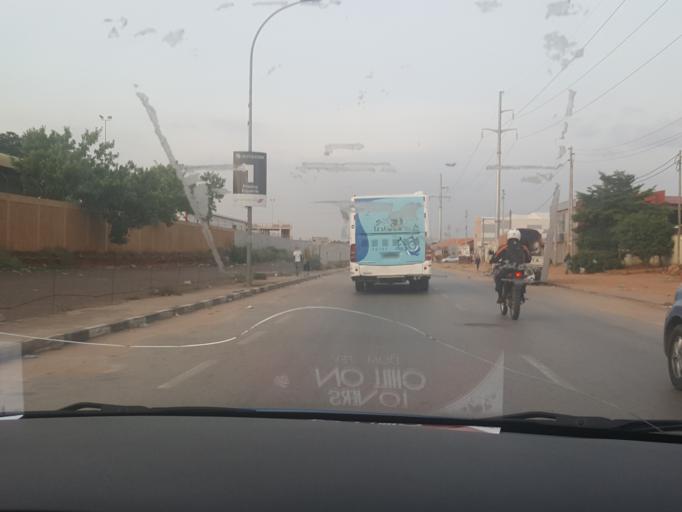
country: AO
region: Luanda
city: Luanda
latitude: -8.9152
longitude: 13.1995
